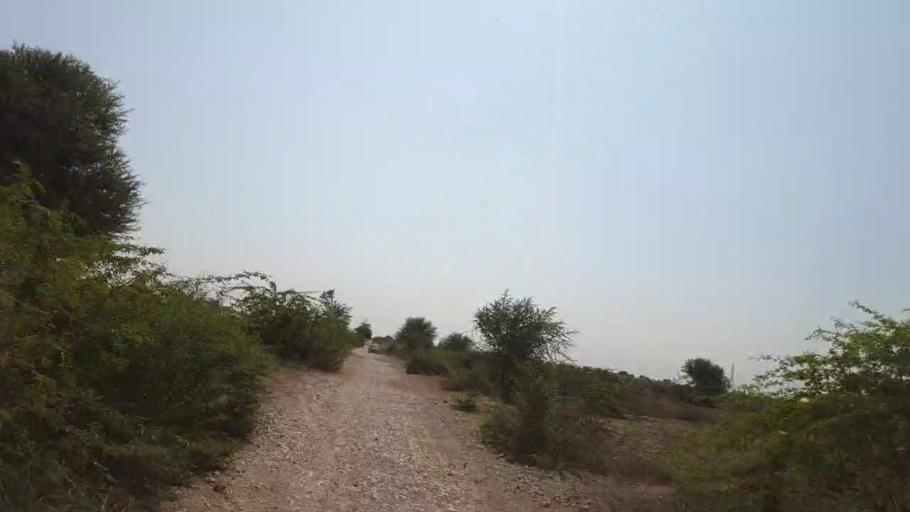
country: PK
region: Sindh
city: Kunri
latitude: 25.0768
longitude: 69.5339
